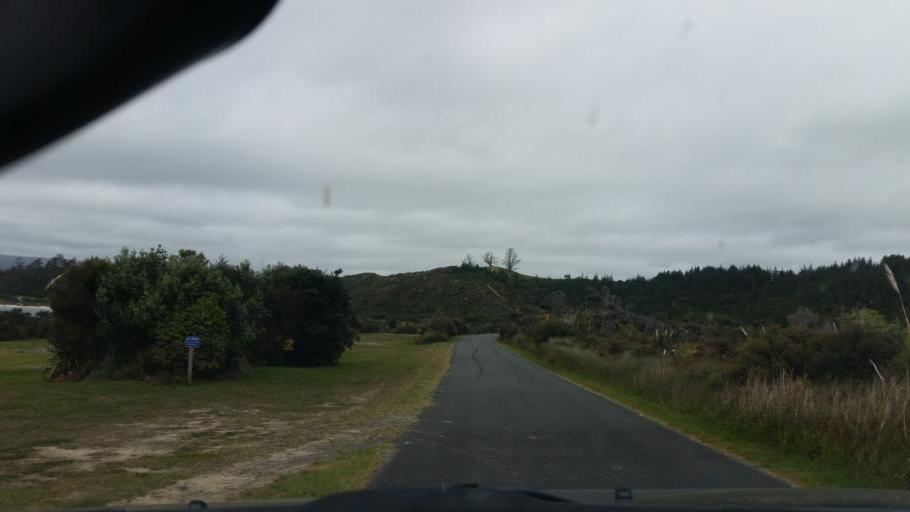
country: NZ
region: Northland
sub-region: Kaipara District
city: Dargaville
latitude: -35.8123
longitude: 173.6562
